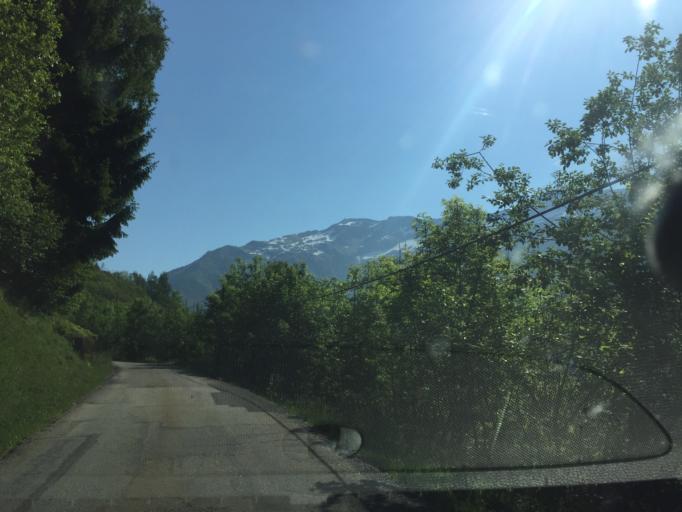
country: FR
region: Rhone-Alpes
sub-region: Departement de la Savoie
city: Sainte-Helene-sur-Isere
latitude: 45.5295
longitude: 6.3515
